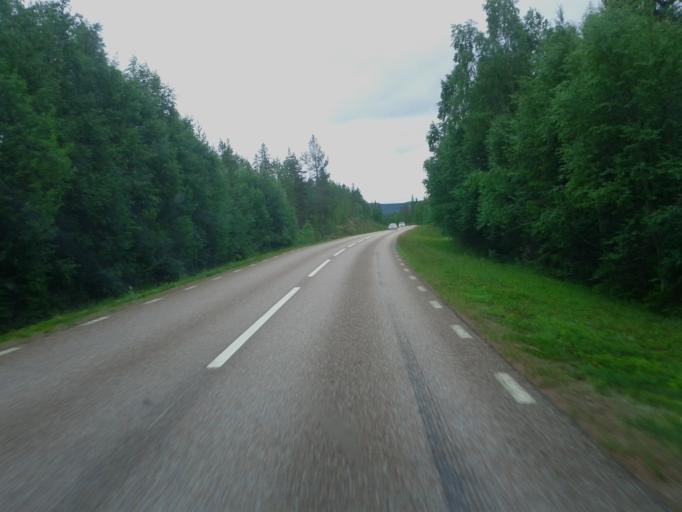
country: NO
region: Hedmark
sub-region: Trysil
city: Innbygda
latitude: 61.7036
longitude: 13.0247
